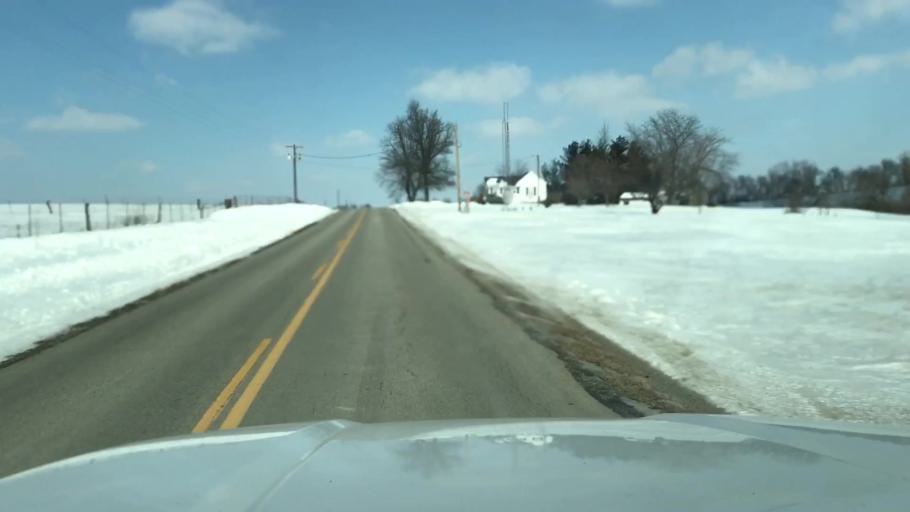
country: US
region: Missouri
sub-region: Nodaway County
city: Maryville
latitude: 40.3469
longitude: -94.7224
